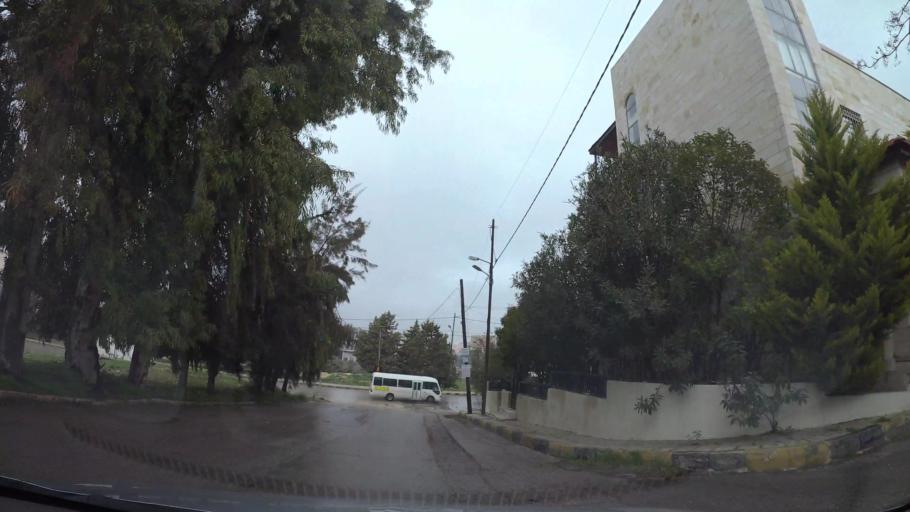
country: JO
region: Amman
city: Al Jubayhah
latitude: 32.0279
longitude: 35.8248
